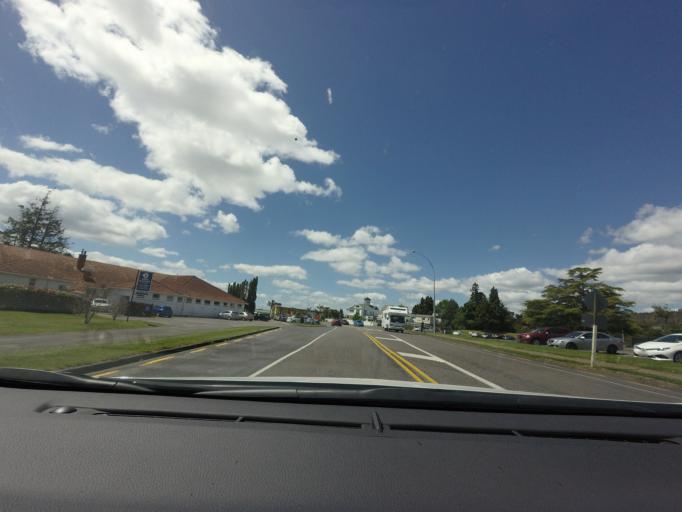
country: NZ
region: Bay of Plenty
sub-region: Rotorua District
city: Rotorua
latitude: -38.1617
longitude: 176.2530
